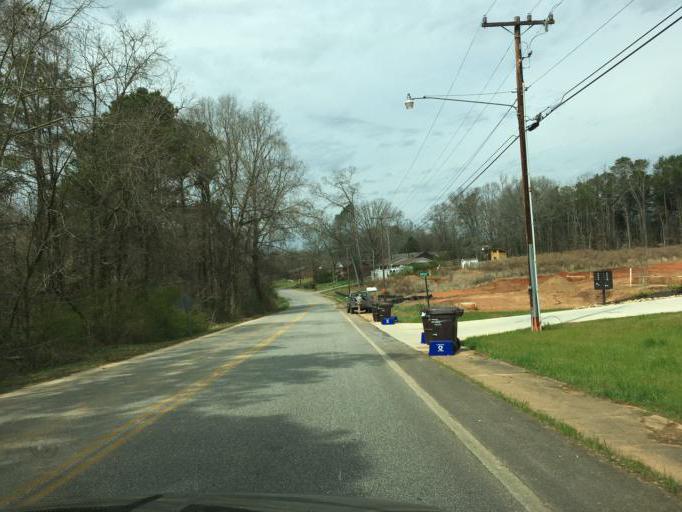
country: US
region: South Carolina
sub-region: Anderson County
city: Pendleton
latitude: 34.6556
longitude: -82.7755
